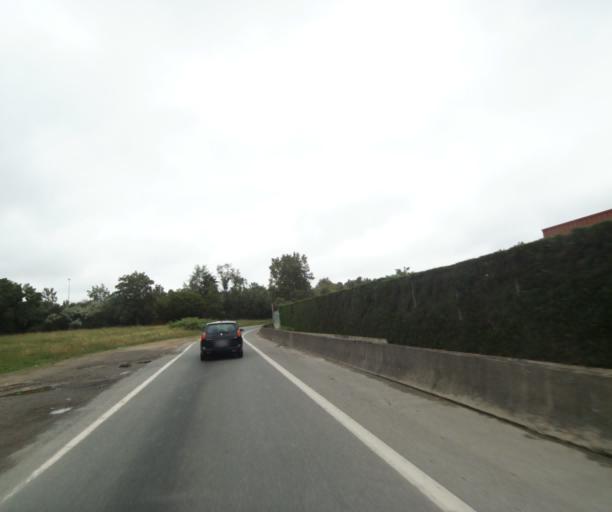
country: FR
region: Rhone-Alpes
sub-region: Departement du Rhone
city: Vaulx-en-Velin
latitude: 45.7893
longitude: 4.9071
